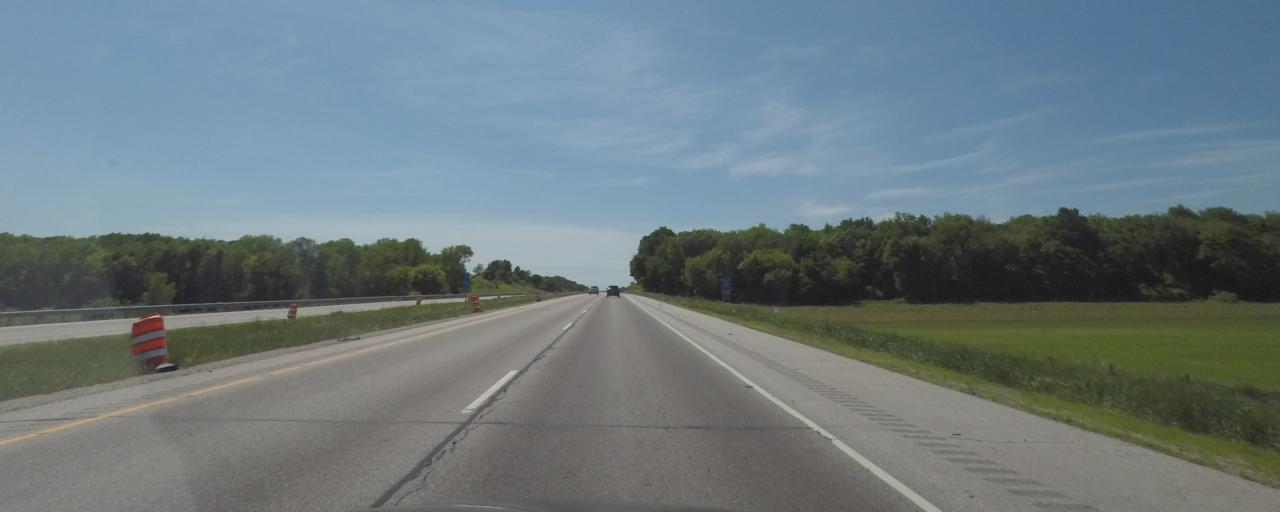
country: US
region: Wisconsin
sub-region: Jefferson County
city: Waterloo
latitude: 43.1110
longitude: -88.9961
